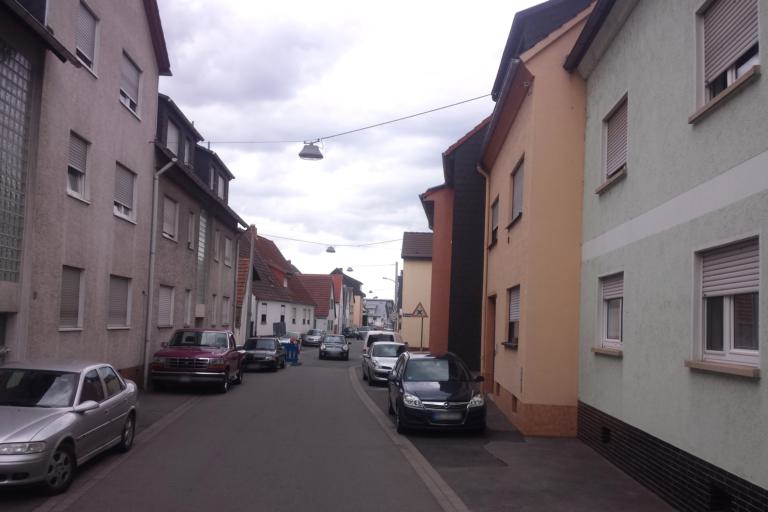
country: DE
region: Hesse
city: Lampertheim
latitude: 49.5464
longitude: 8.4392
